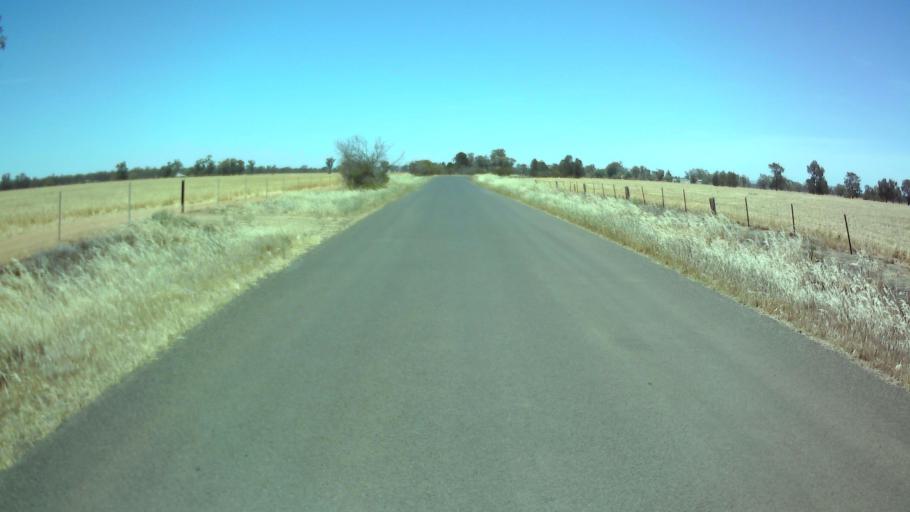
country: AU
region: New South Wales
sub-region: Weddin
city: Grenfell
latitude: -34.0541
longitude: 147.7810
